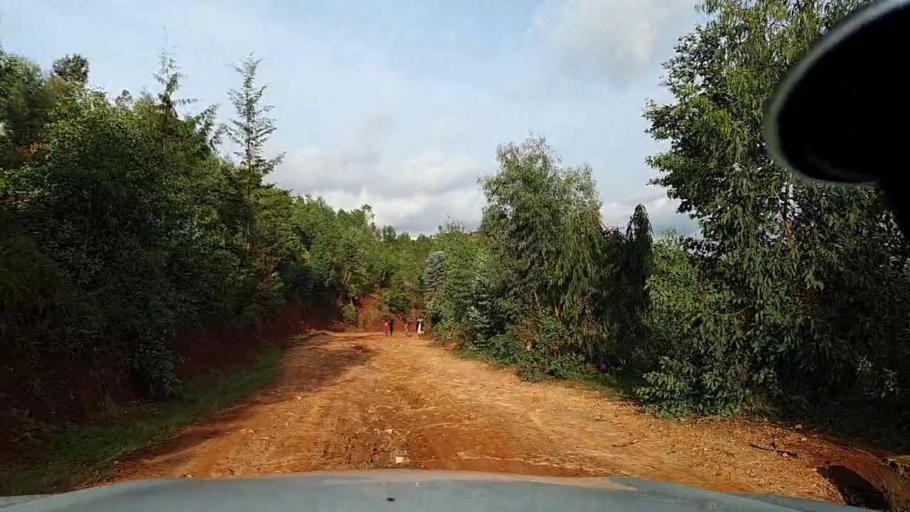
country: RW
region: Southern Province
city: Gitarama
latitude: -2.1862
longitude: 29.5677
